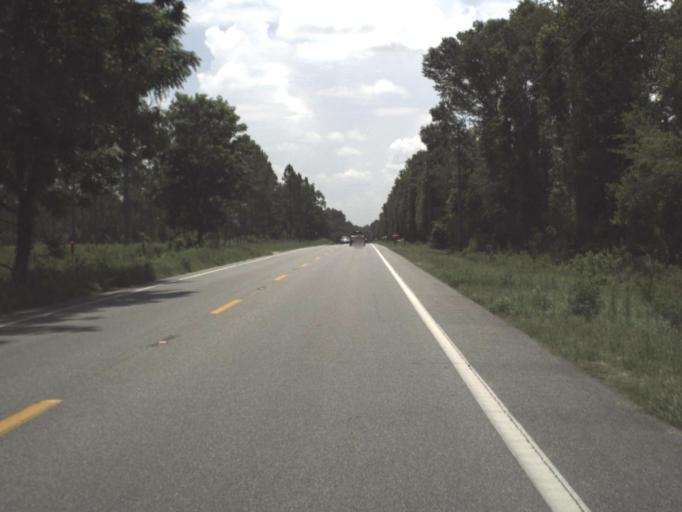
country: US
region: Florida
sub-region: Madison County
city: Madison
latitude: 30.4422
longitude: -83.3310
